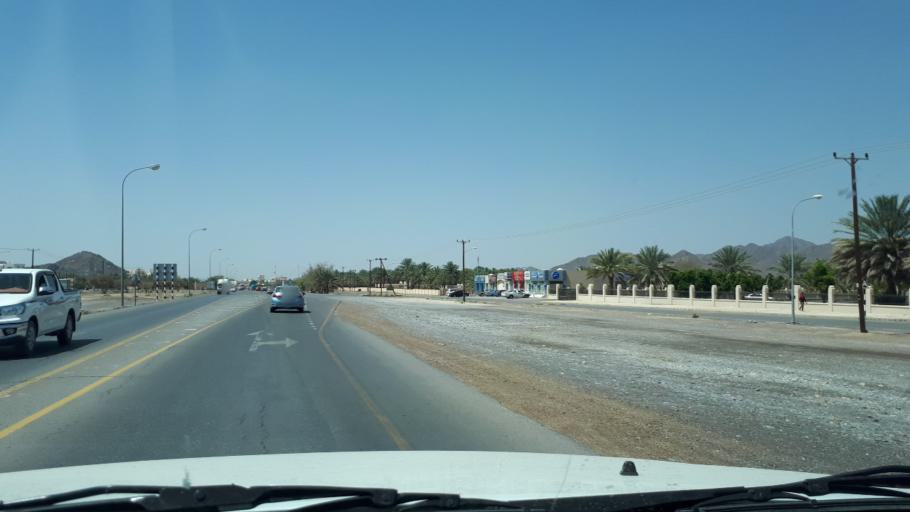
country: OM
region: Muhafazat ad Dakhiliyah
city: Bahla'
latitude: 22.9932
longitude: 57.3135
